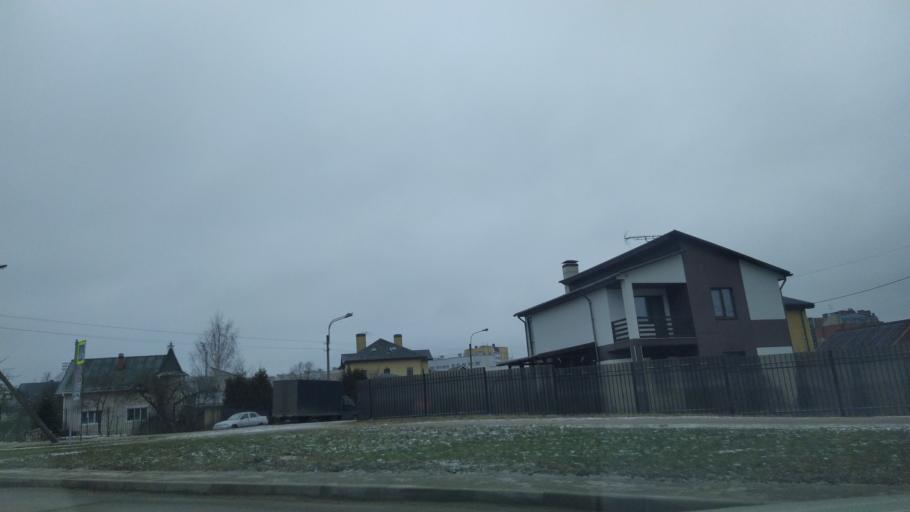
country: RU
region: St.-Petersburg
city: Pushkin
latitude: 59.7340
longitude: 30.4104
